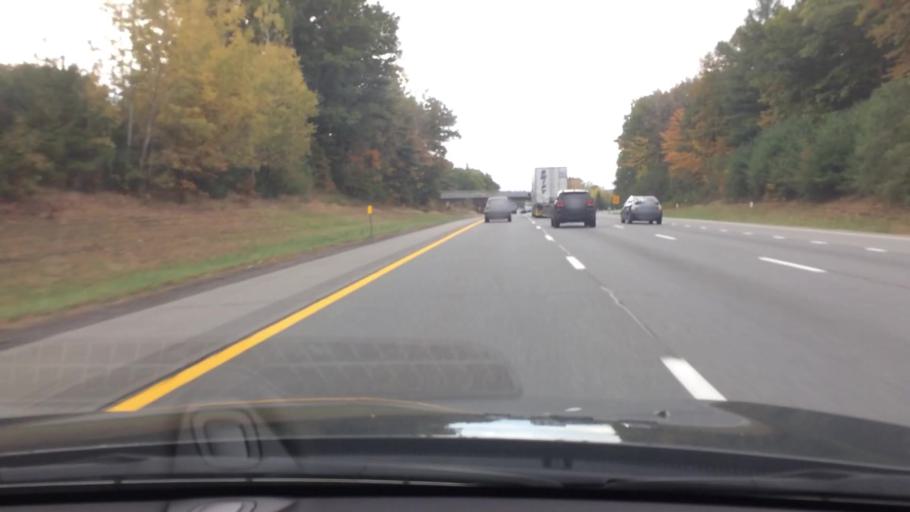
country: US
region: New York
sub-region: Saratoga County
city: Country Knolls
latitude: 42.9050
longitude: -73.7885
